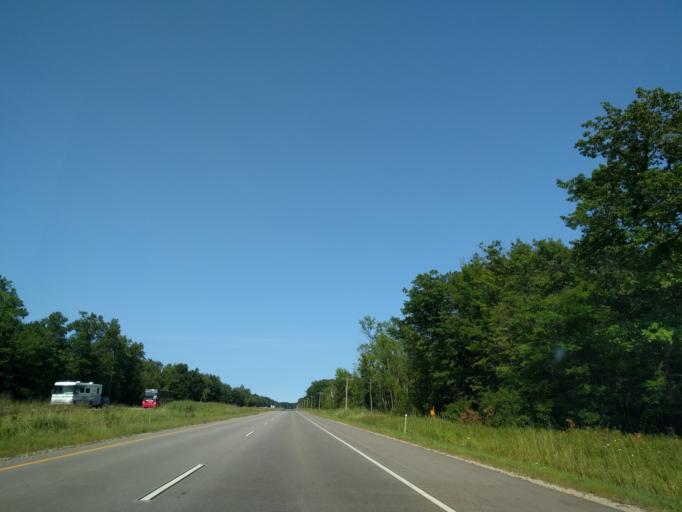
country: US
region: Wisconsin
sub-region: Oconto County
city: Oconto
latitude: 44.8383
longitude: -87.9152
